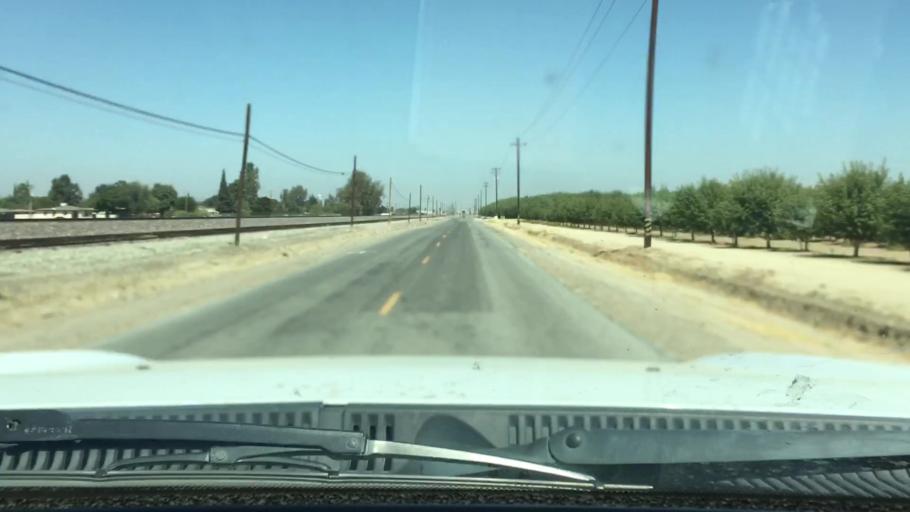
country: US
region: California
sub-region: Kern County
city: Wasco
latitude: 35.5703
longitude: -119.3318
